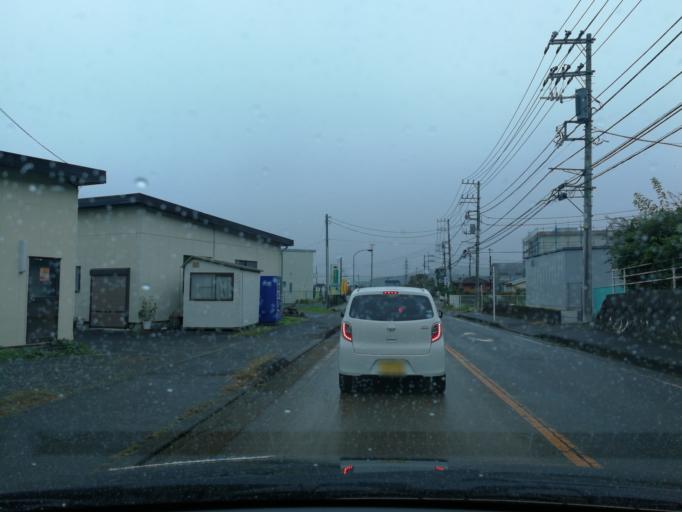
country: JP
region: Yamanashi
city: Uenohara
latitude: 35.6076
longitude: 139.2176
